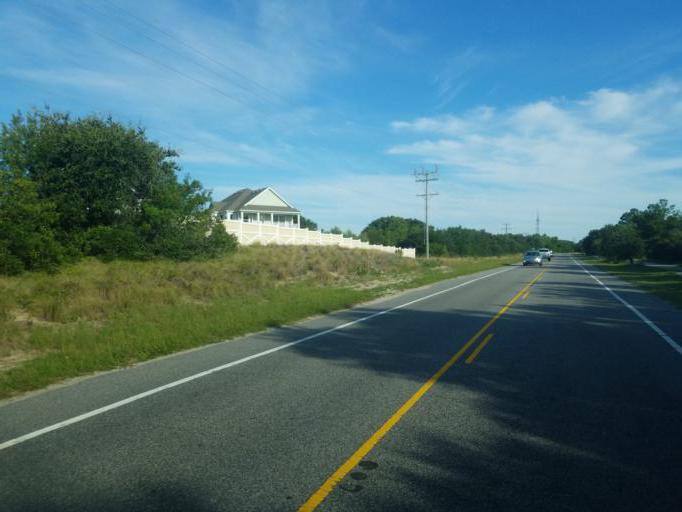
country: US
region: North Carolina
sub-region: Dare County
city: Southern Shores
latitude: 36.3139
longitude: -75.8120
